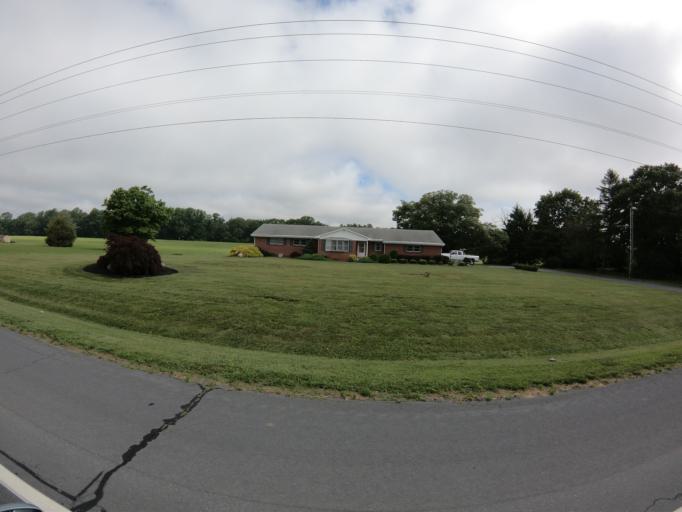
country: US
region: Delaware
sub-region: Kent County
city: Felton
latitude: 39.0059
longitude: -75.5442
